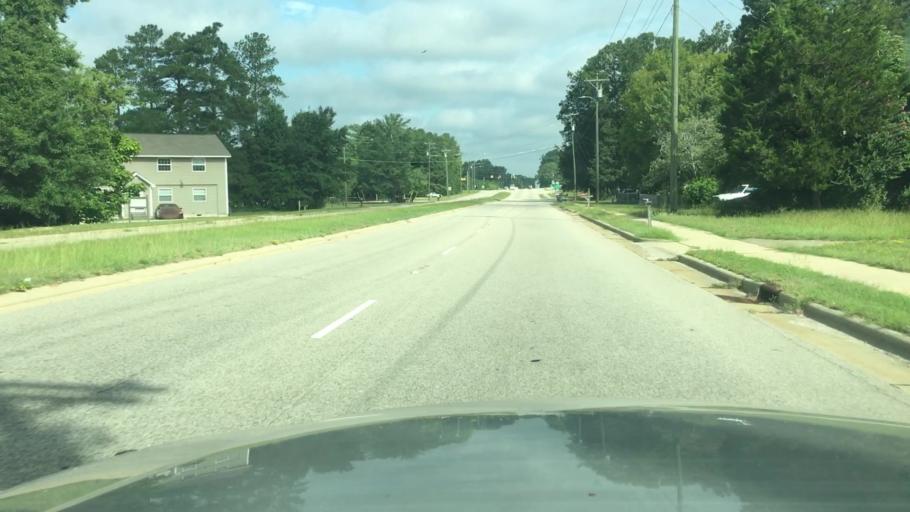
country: US
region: North Carolina
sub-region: Cumberland County
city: Hope Mills
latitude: 34.9929
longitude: -78.9636
